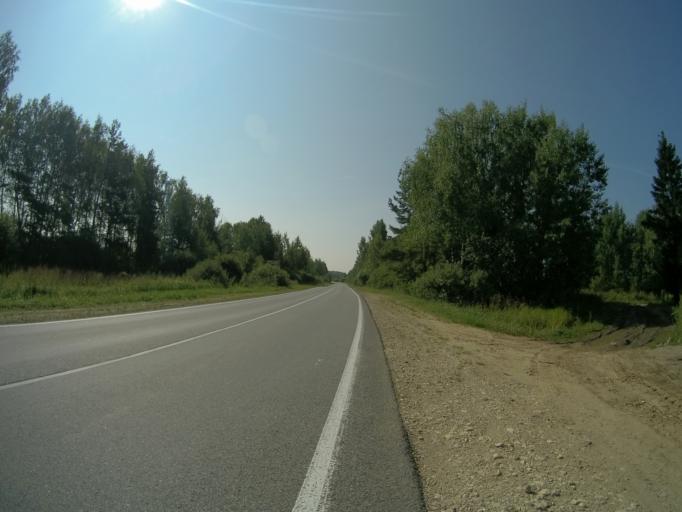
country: RU
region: Vladimir
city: Golovino
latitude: 55.9111
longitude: 40.6070
